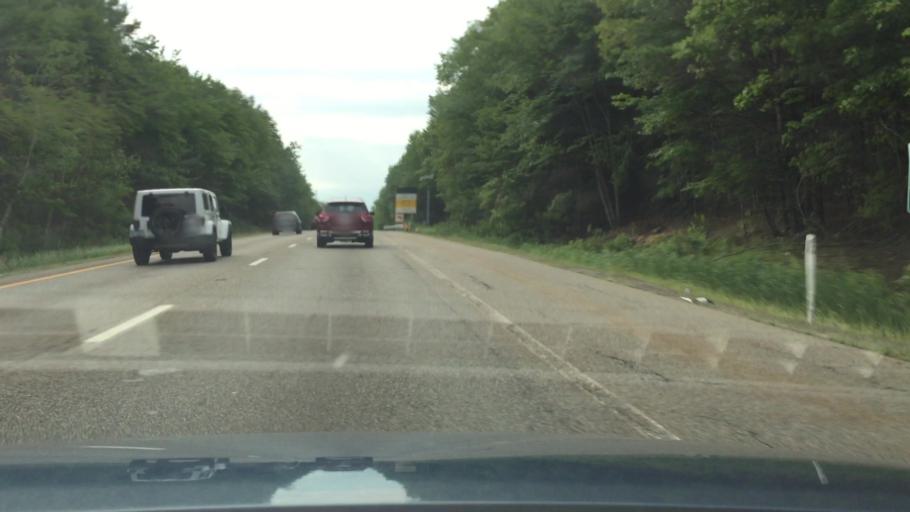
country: US
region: Massachusetts
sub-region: Plymouth County
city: Hanover
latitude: 42.1322
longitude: -70.8098
